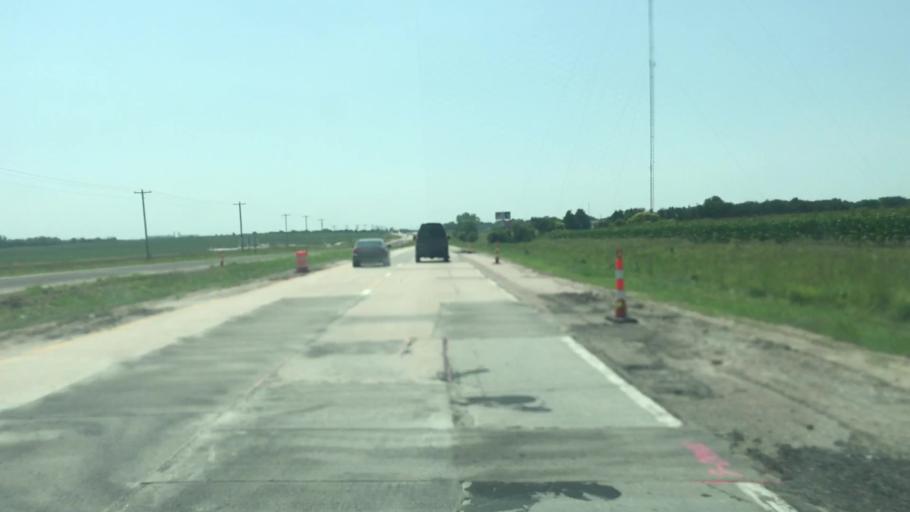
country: US
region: Nebraska
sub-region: Adams County
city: Hastings
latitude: 40.6532
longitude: -98.3825
